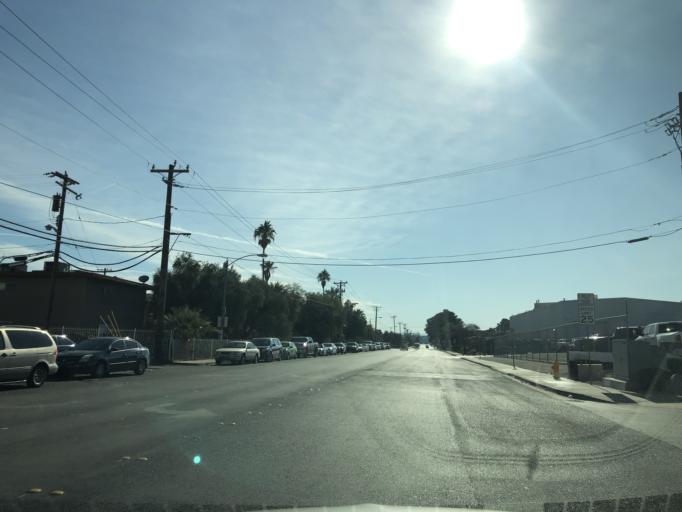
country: US
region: Nevada
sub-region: Clark County
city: Winchester
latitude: 36.1296
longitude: -115.1415
